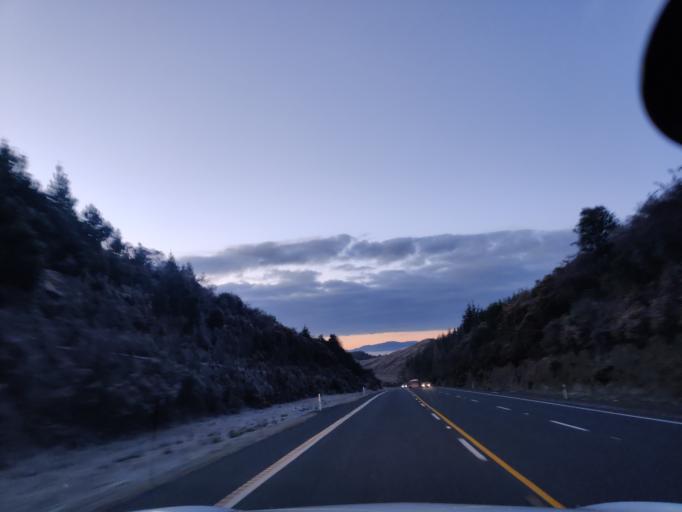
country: NZ
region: Waikato
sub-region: South Waikato District
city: Tokoroa
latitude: -38.3224
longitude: 175.9867
